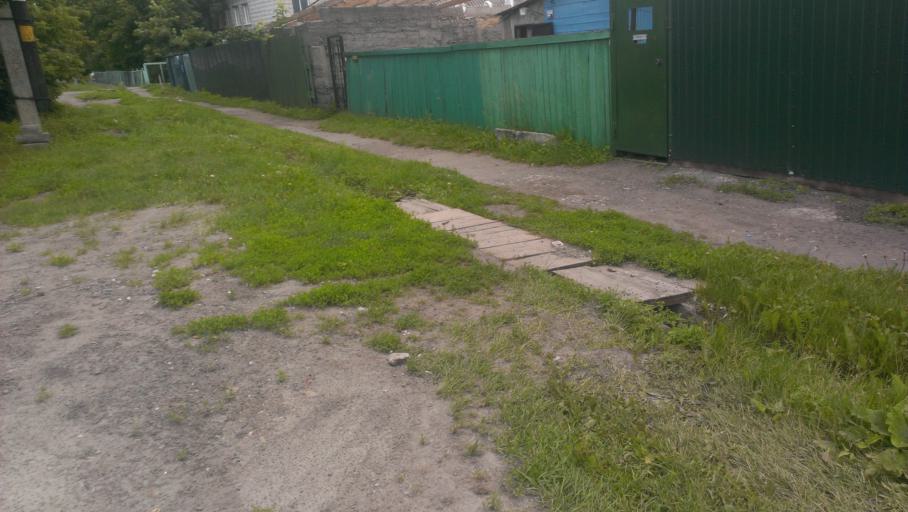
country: RU
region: Altai Krai
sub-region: Gorod Barnaulskiy
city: Barnaul
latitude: 53.3397
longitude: 83.7303
